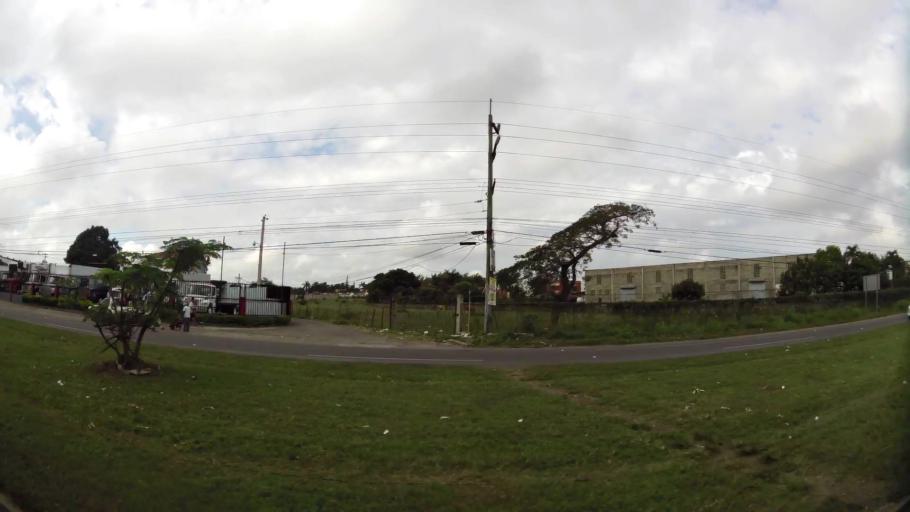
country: DO
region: Santiago
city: Licey al Medio
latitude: 19.4193
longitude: -70.6472
